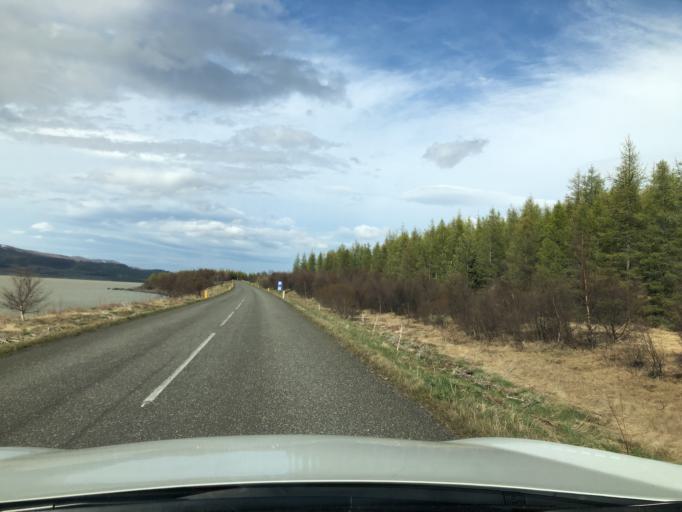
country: IS
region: East
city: Egilsstadir
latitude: 65.1273
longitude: -14.6947
